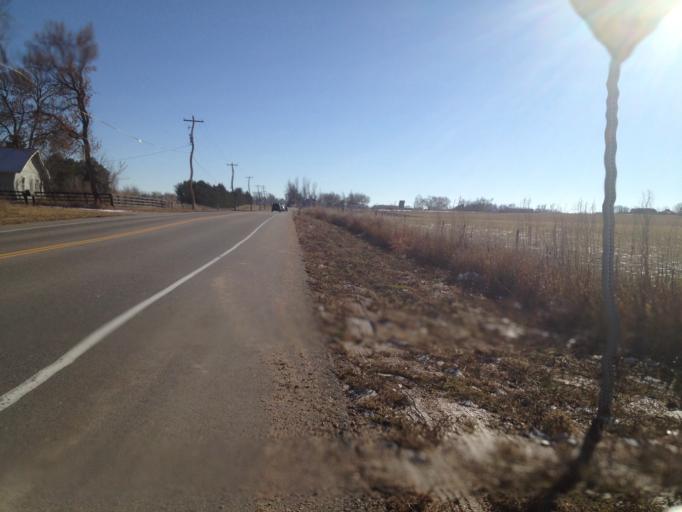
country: US
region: Colorado
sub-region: Boulder County
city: Gunbarrel
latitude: 40.0443
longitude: -105.1313
